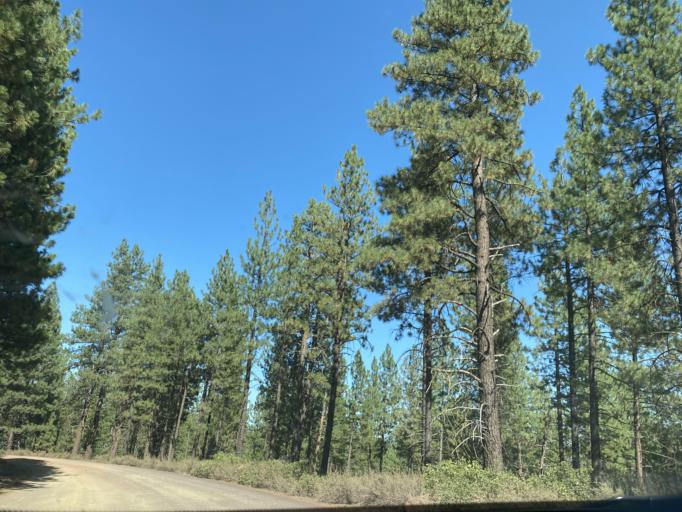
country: US
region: Oregon
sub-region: Deschutes County
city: Sunriver
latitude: 43.8707
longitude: -121.4758
